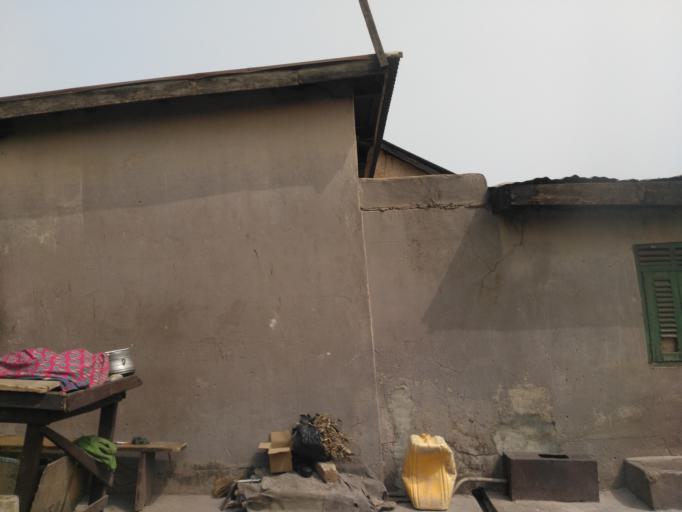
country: GH
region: Ashanti
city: Kumasi
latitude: 6.6996
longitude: -1.6042
